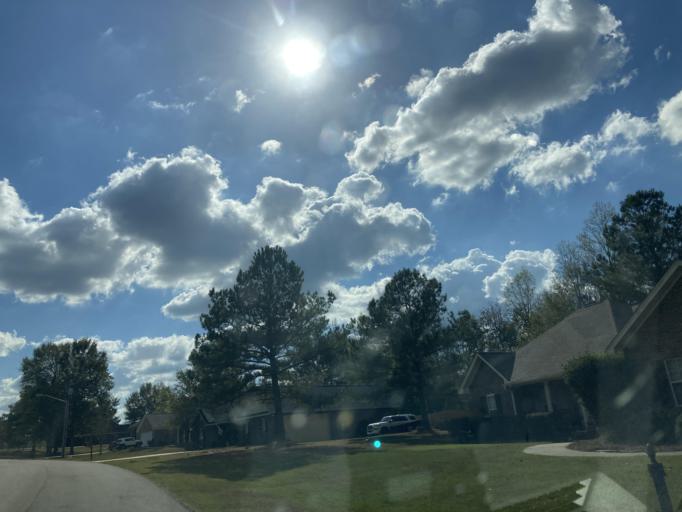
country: US
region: Mississippi
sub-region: Lamar County
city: Sumrall
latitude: 31.3998
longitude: -89.5365
